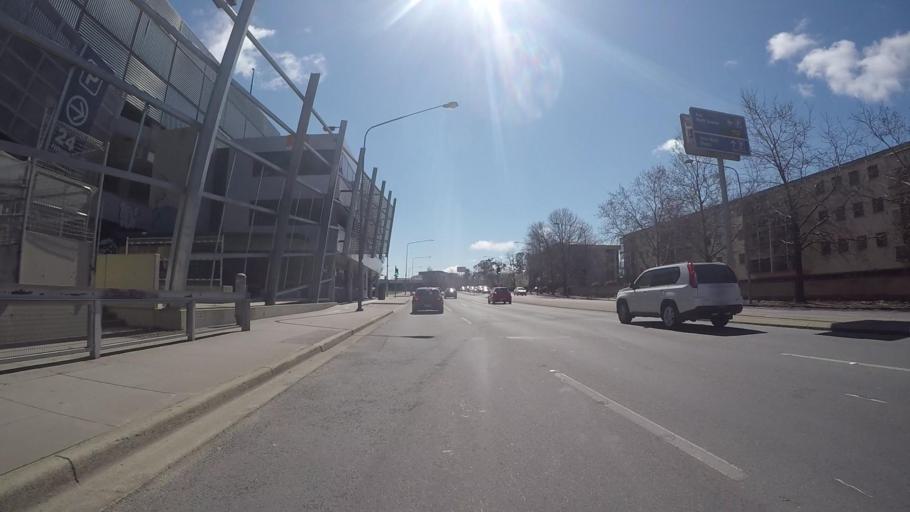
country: AU
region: Australian Capital Territory
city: Canberra
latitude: -35.2780
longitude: 149.1347
